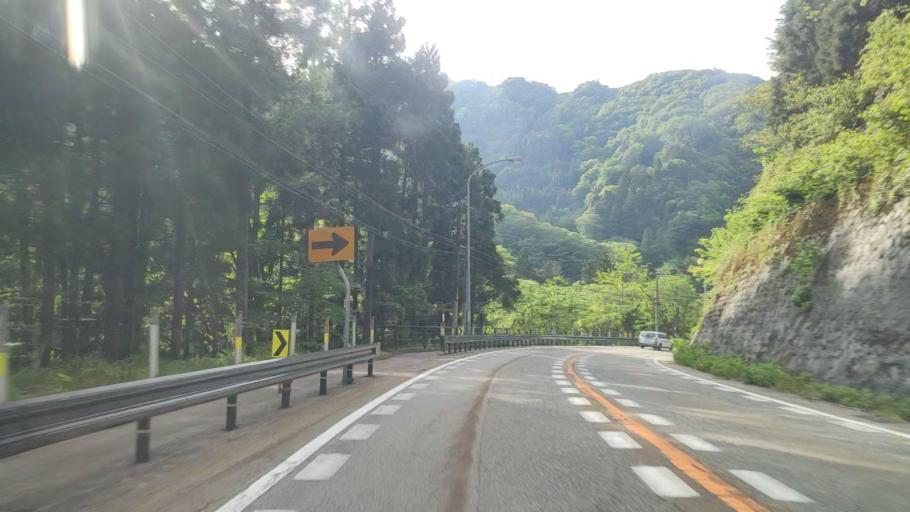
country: JP
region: Toyama
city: Yatsuomachi-higashikumisaka
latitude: 36.4365
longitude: 137.2741
